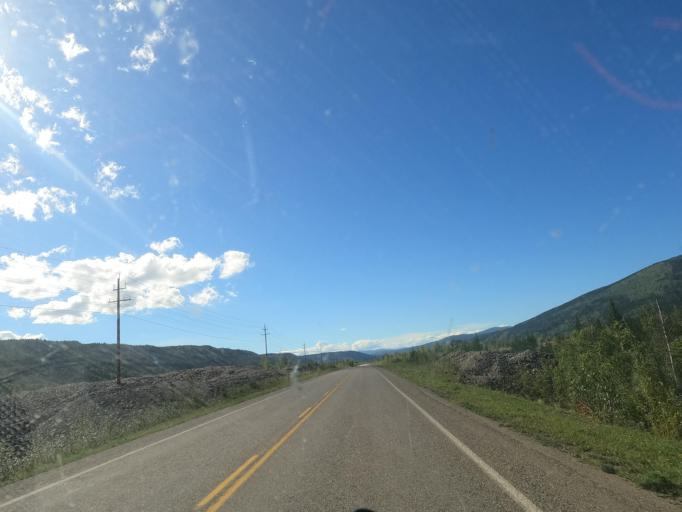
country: CA
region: Yukon
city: Dawson City
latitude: 64.0342
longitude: -139.2702
